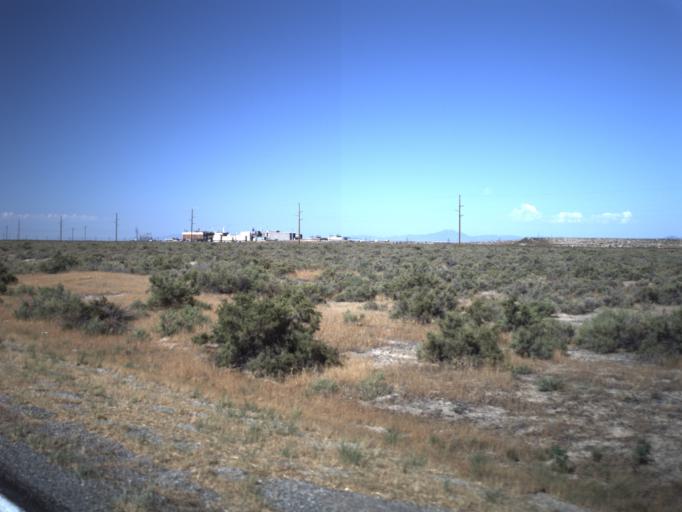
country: US
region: Utah
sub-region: Millard County
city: Delta
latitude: 39.4718
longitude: -112.4226
